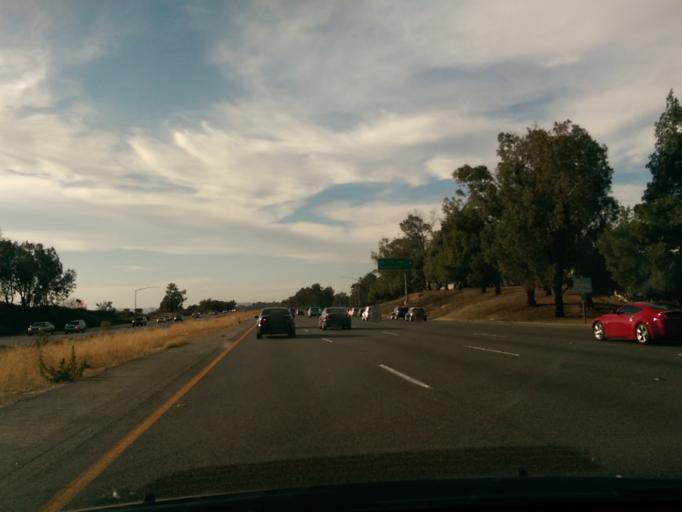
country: US
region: California
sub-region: Riverside County
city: Temecula
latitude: 33.4751
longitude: -117.1386
